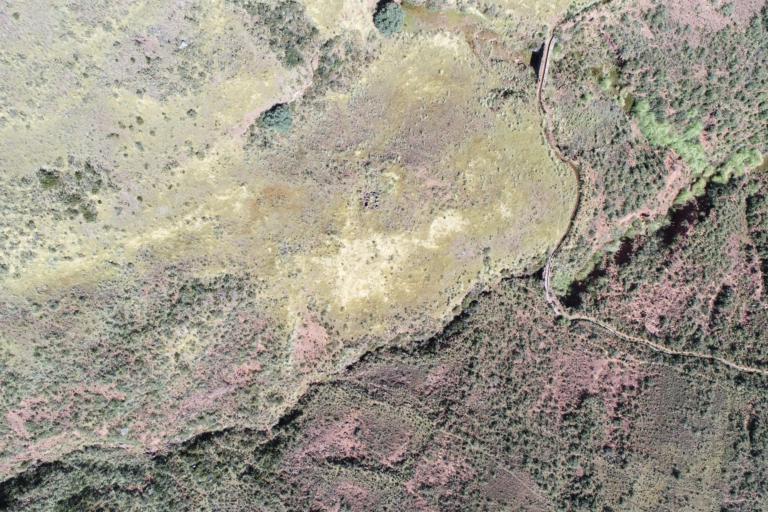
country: BO
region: La Paz
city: Tiahuanaco
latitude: -16.6092
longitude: -68.7599
